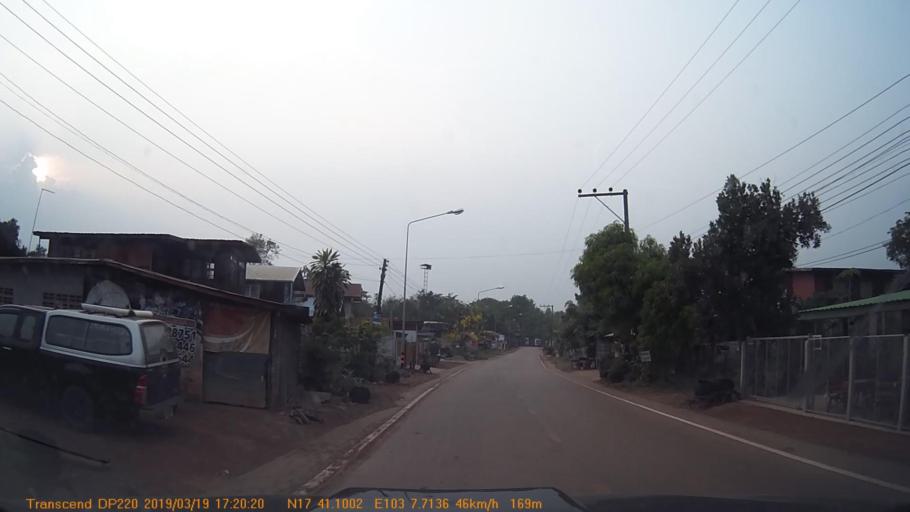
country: TH
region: Changwat Udon Thani
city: Ban Dung
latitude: 17.6852
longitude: 103.1280
